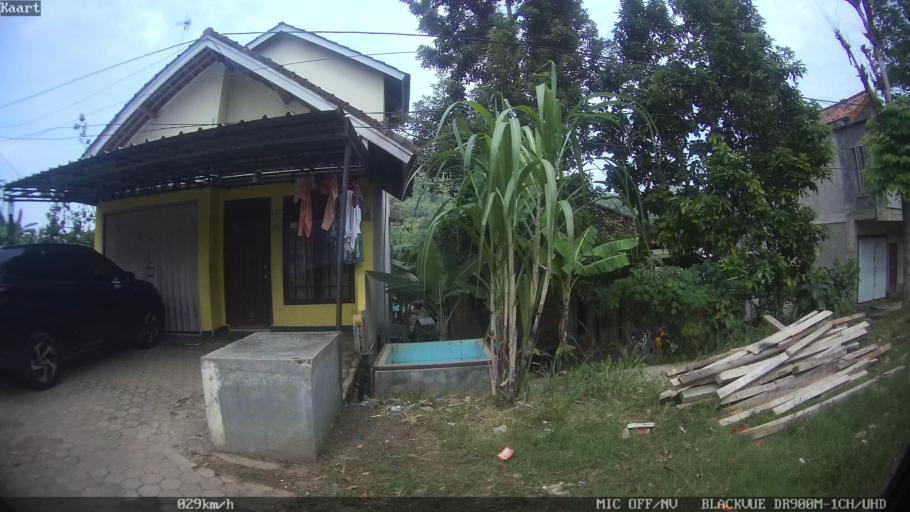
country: ID
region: Lampung
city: Bandarlampung
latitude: -5.4423
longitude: 105.2411
